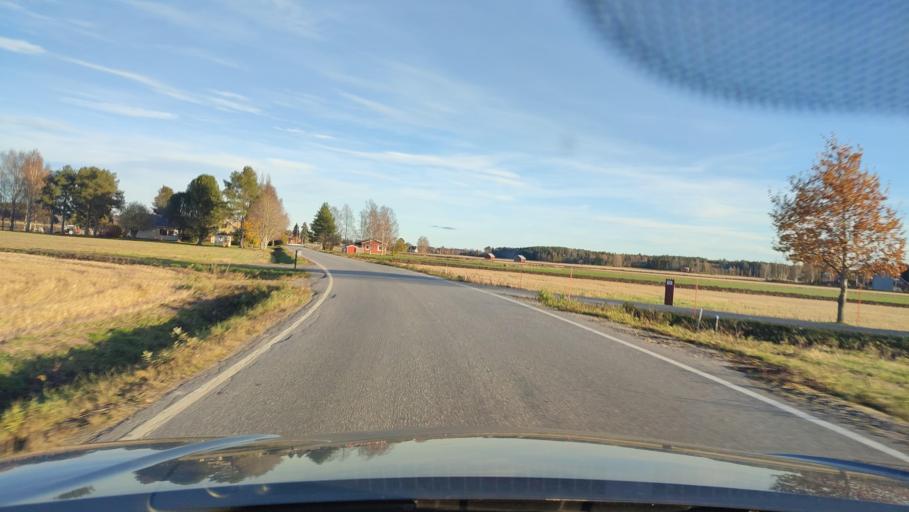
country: FI
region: Ostrobothnia
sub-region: Vaasa
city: Teeriniemi
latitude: 63.0008
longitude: 21.6893
